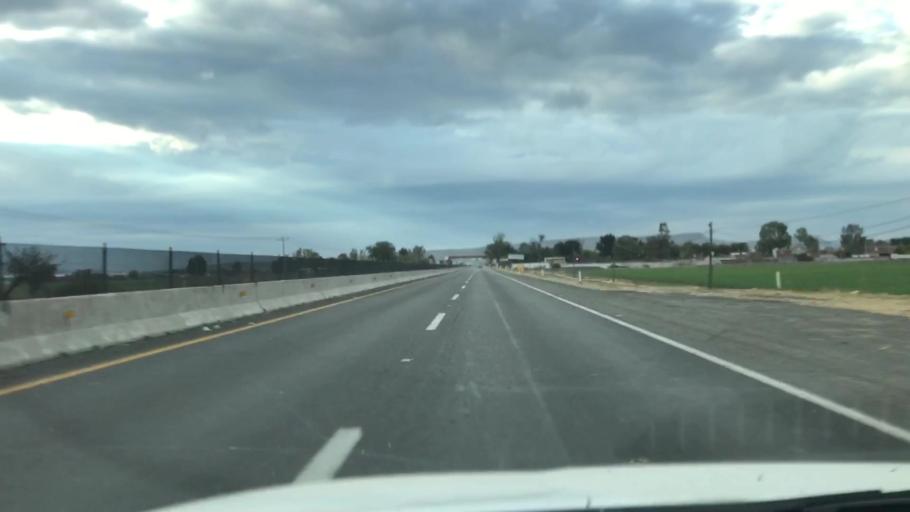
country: MX
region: Guanajuato
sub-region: Penjamo
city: Estacion la Piedad
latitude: 20.3872
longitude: -101.9161
